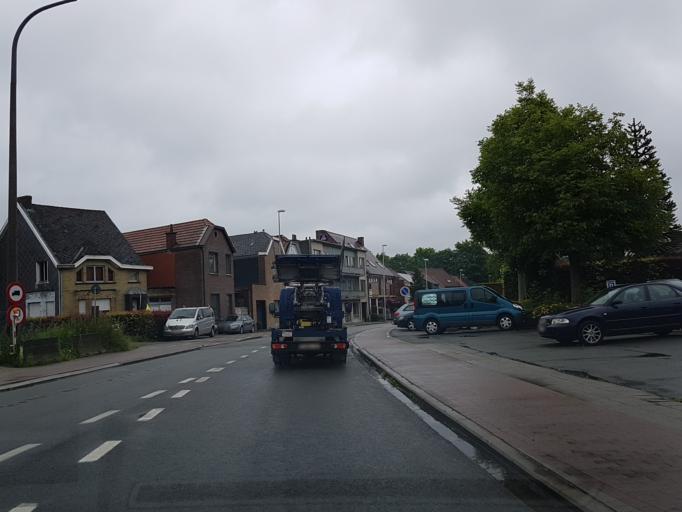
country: BE
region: Flanders
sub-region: Provincie Oost-Vlaanderen
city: Aalst
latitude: 50.9302
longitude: 4.0180
